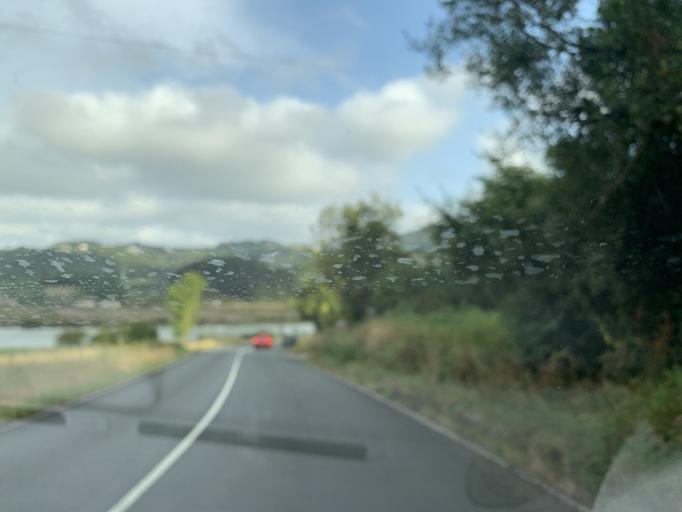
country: ES
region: Asturias
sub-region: Province of Asturias
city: Villaviciosa
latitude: 43.5021
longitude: -5.4280
